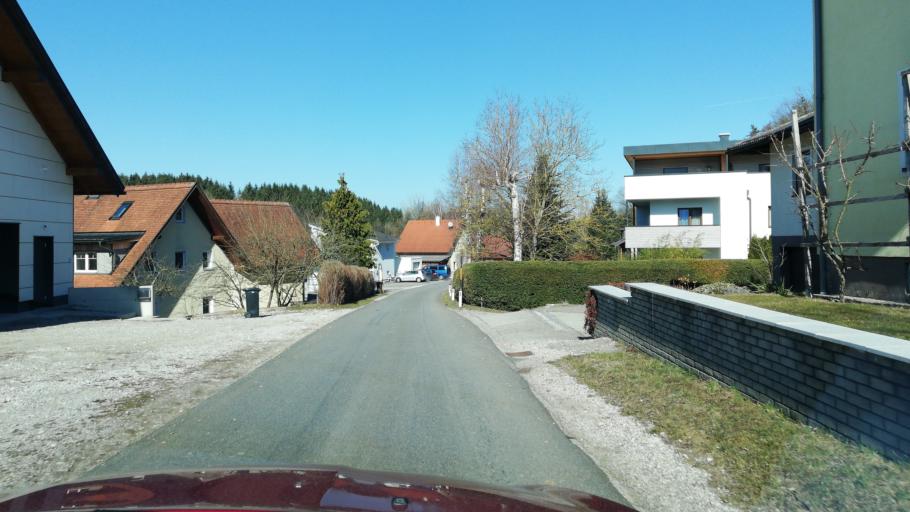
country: AT
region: Upper Austria
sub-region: Politischer Bezirk Vocklabruck
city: Aurach am Hongar
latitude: 47.9608
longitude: 13.6963
